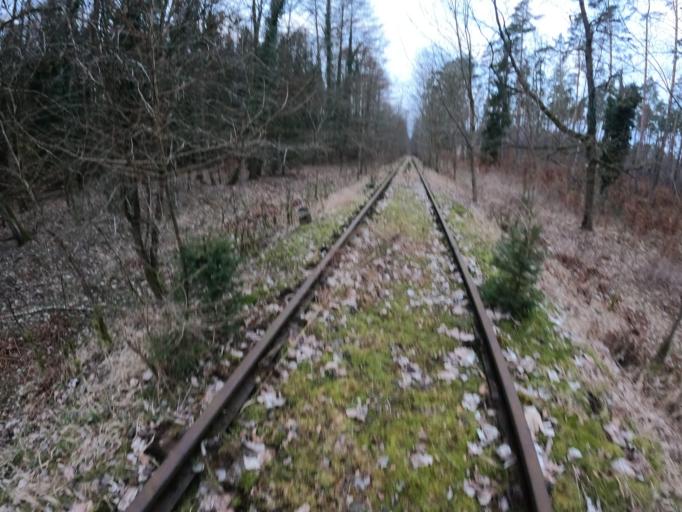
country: PL
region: West Pomeranian Voivodeship
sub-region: Powiat kamienski
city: Golczewo
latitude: 53.8257
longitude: 15.0156
